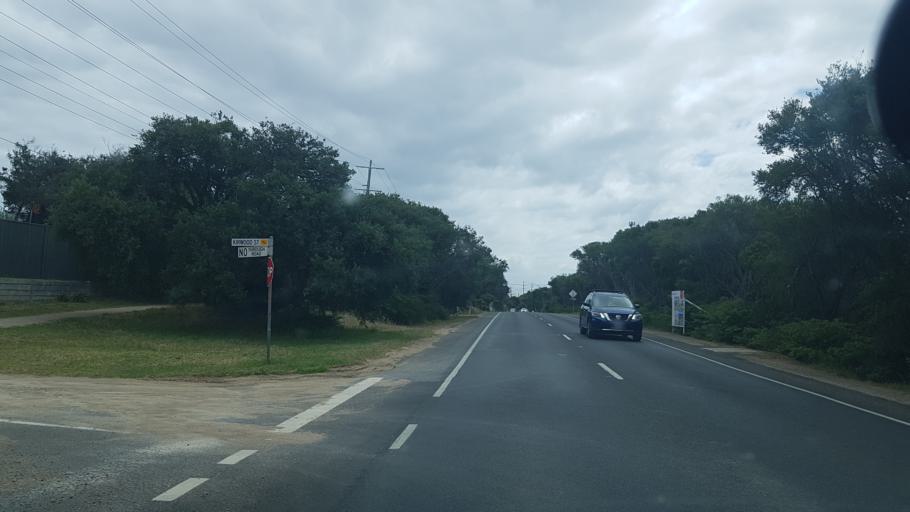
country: AU
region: Victoria
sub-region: Mornington Peninsula
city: Blairgowrie
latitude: -38.3679
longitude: 144.7699
